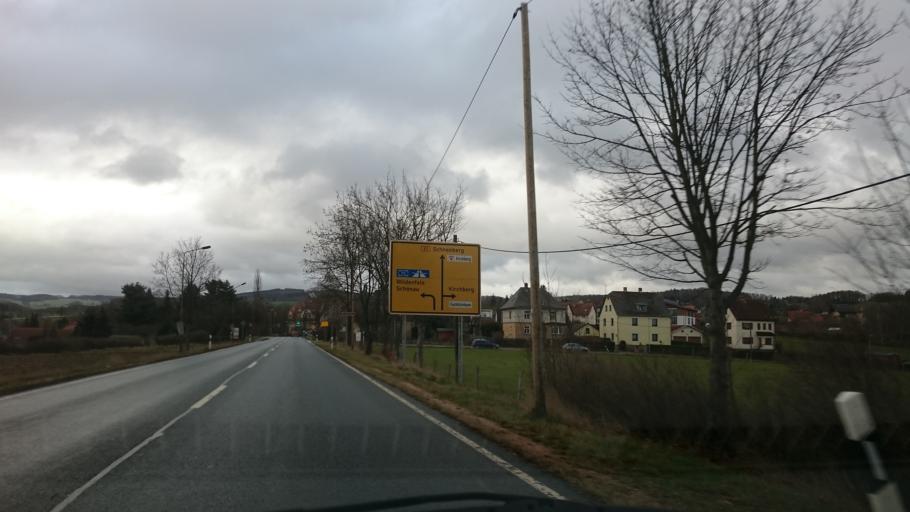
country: DE
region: Saxony
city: Kirchberg
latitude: 50.6520
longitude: 12.5589
